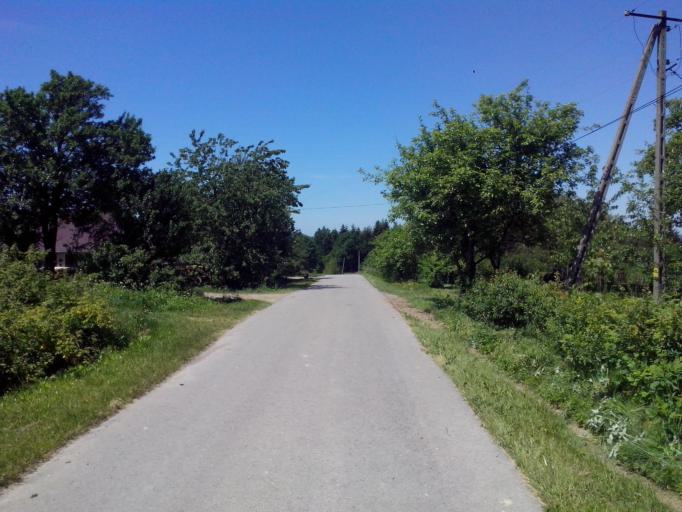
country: PL
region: Subcarpathian Voivodeship
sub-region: Powiat strzyzowski
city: Wysoka Strzyzowska
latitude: 49.8173
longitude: 21.7707
